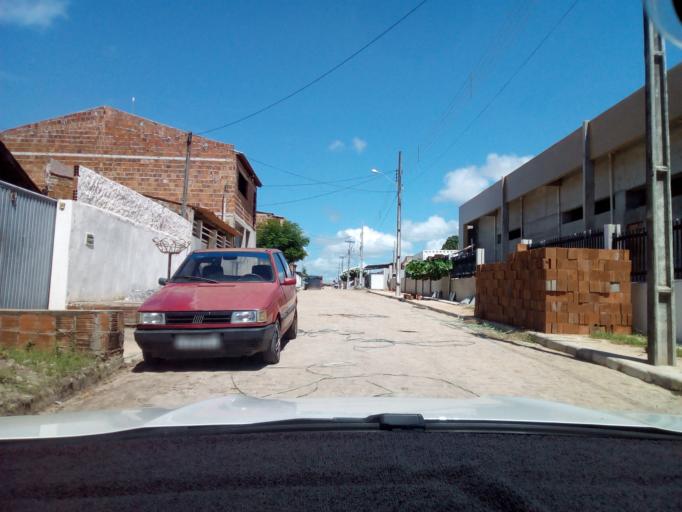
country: BR
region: Paraiba
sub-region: Joao Pessoa
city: Joao Pessoa
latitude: -7.1731
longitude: -34.8290
